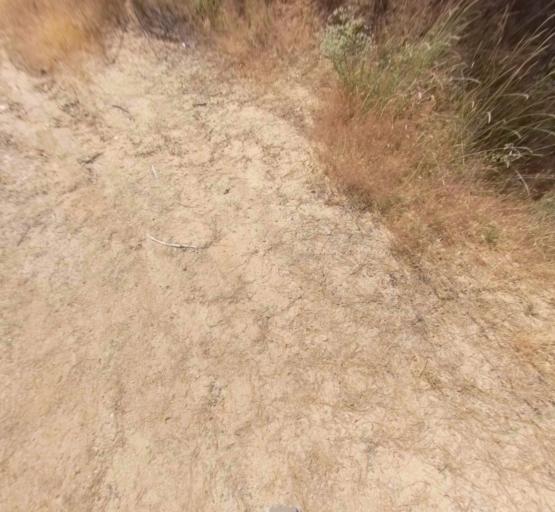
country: US
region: California
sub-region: Madera County
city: Oakhurst
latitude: 37.3738
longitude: -119.6255
